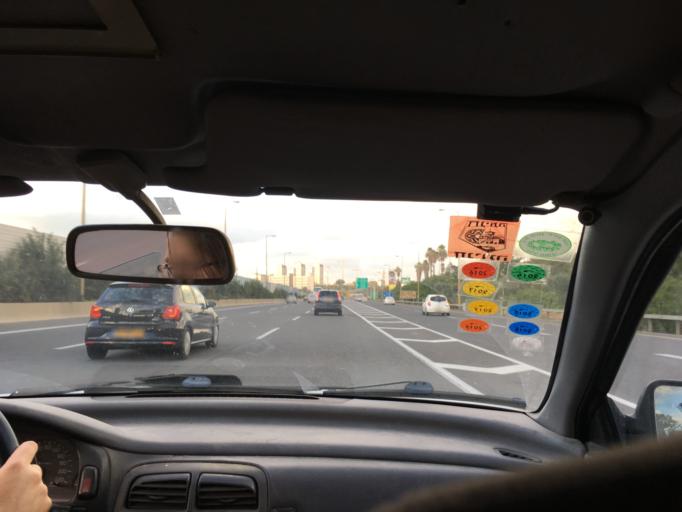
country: IL
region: Tel Aviv
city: Ramat Gan
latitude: 32.0951
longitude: 34.8021
